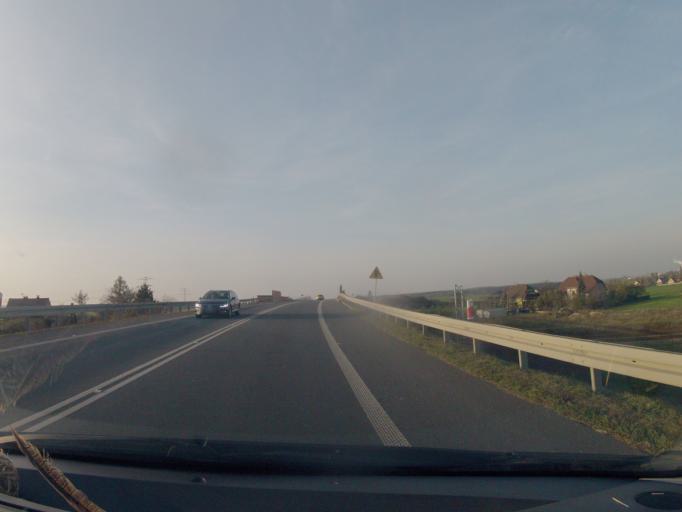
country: PL
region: Opole Voivodeship
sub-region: Powiat strzelecki
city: Strzelce Opolskie
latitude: 50.5216
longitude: 18.2790
